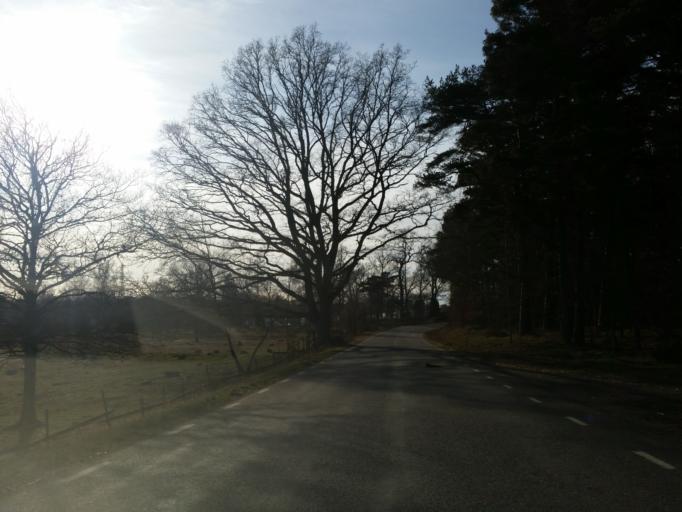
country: SE
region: Kalmar
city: Faerjestaden
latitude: 56.7741
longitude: 16.4618
